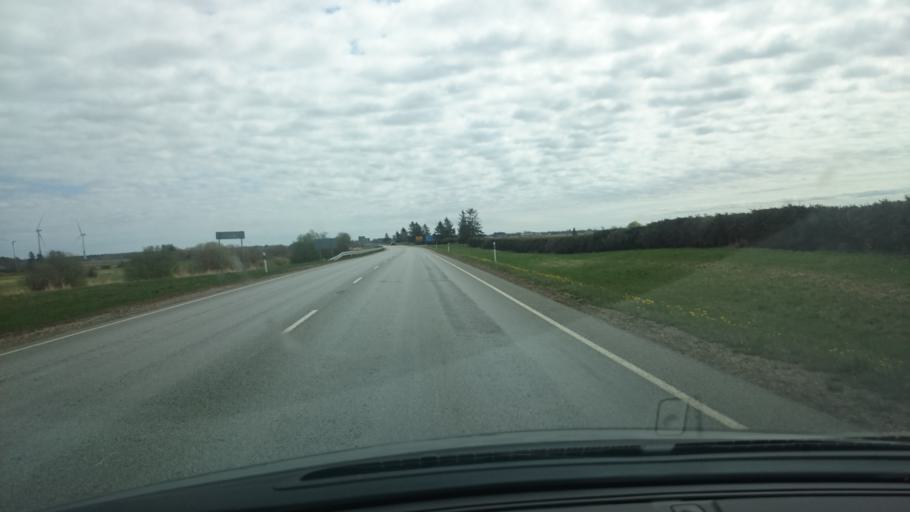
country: EE
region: Ida-Virumaa
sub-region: Aseri vald
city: Aseri
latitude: 59.4437
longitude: 26.7836
